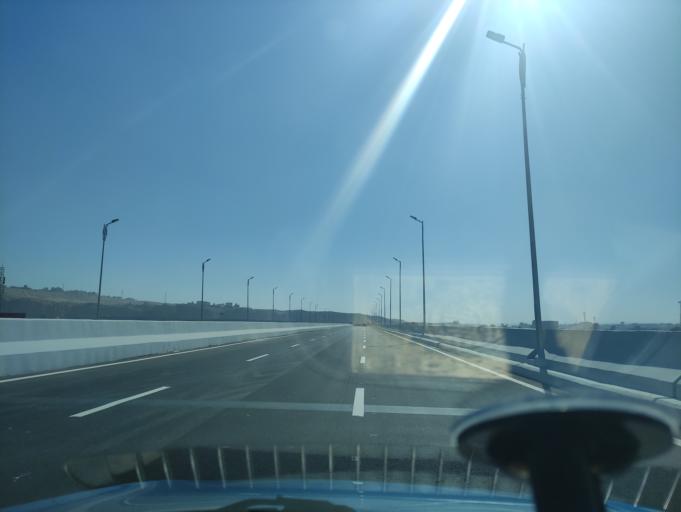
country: EG
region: Al Jizah
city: Al Jizah
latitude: 30.0078
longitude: 31.2599
